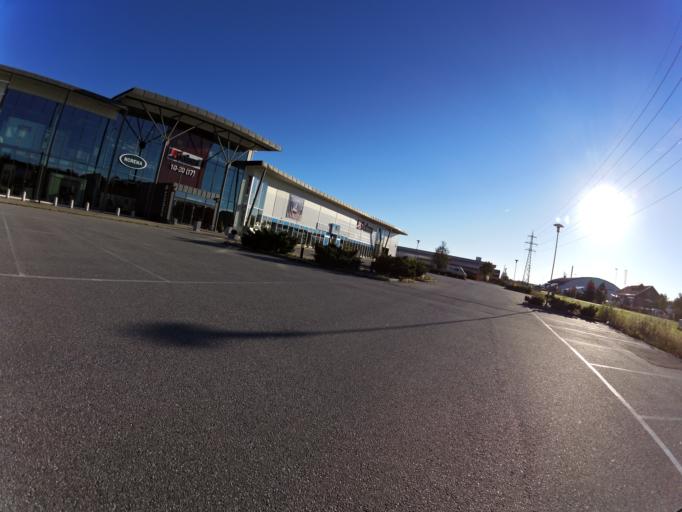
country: NO
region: Ostfold
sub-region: Fredrikstad
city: Fredrikstad
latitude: 59.2545
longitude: 10.9998
